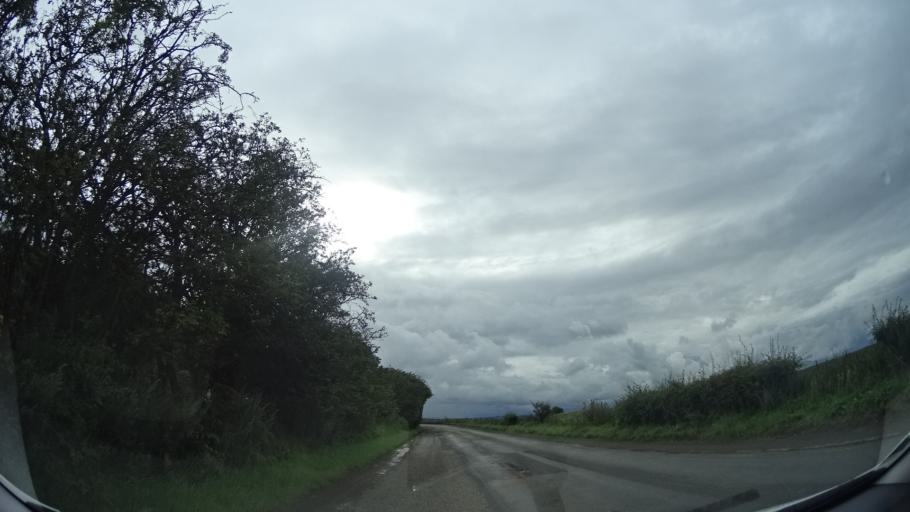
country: GB
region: Scotland
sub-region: West Lothian
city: Kirknewton
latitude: 55.9010
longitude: -3.4340
